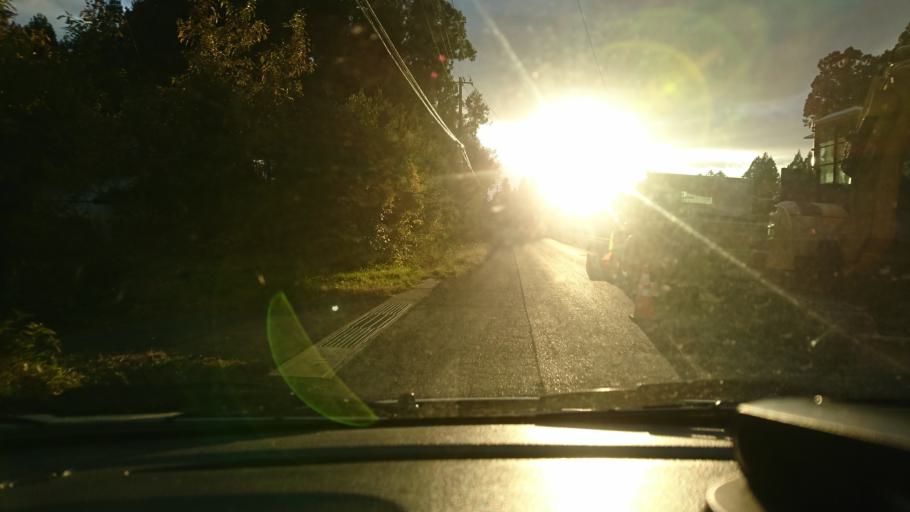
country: JP
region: Iwate
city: Ichinoseki
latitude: 38.7921
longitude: 141.1895
